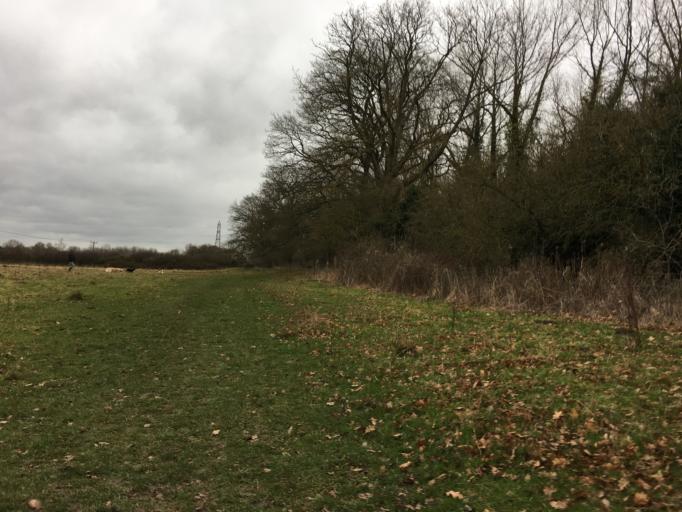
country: GB
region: England
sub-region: Warwickshire
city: Rugby
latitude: 52.3989
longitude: -1.2600
